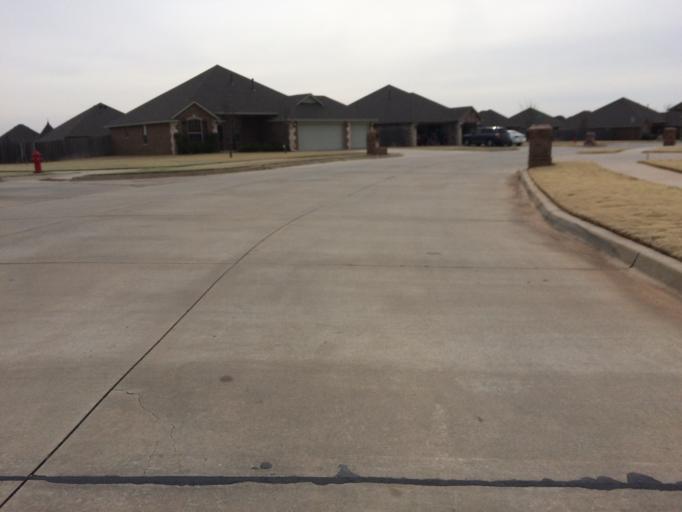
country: US
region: Oklahoma
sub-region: Cleveland County
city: Hall Park
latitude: 35.2140
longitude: -97.3921
